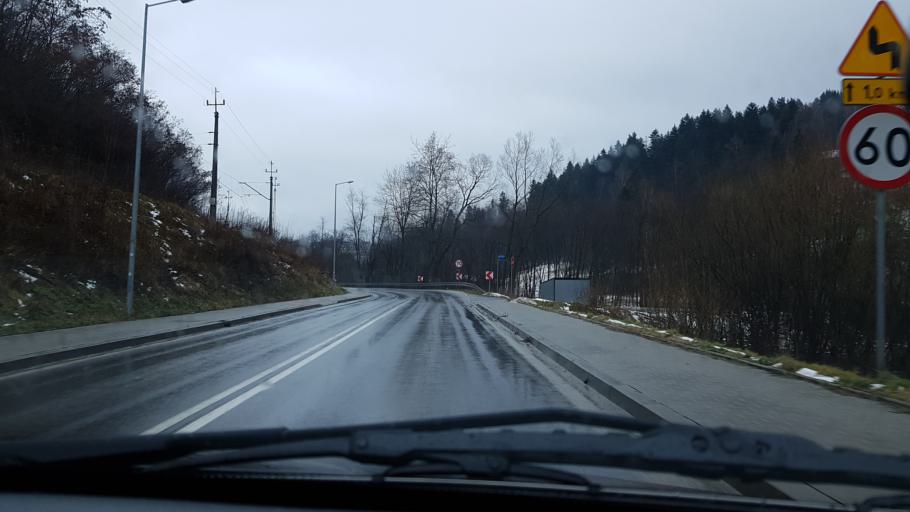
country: PL
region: Lesser Poland Voivodeship
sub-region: Powiat nowotarski
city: Raba Wyzna
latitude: 49.5483
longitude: 19.8842
